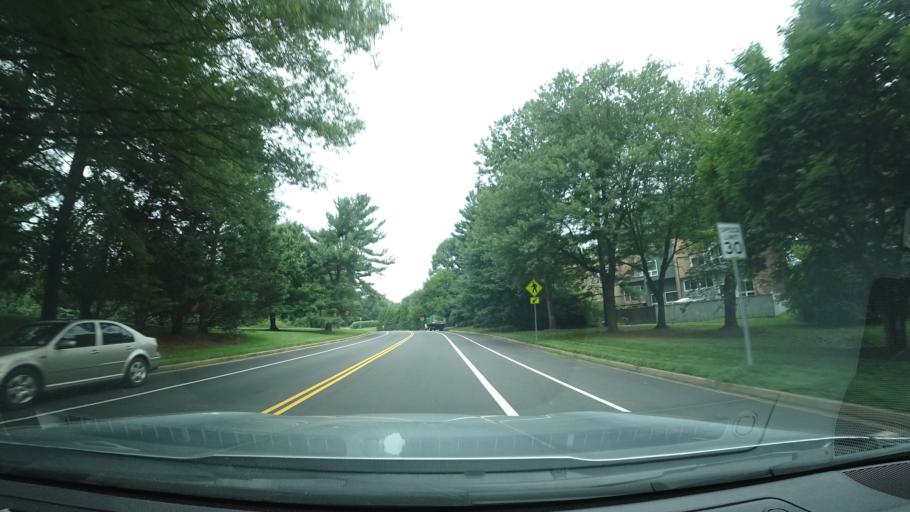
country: US
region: Virginia
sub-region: Fairfax County
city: Reston
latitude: 38.9562
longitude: -77.3428
